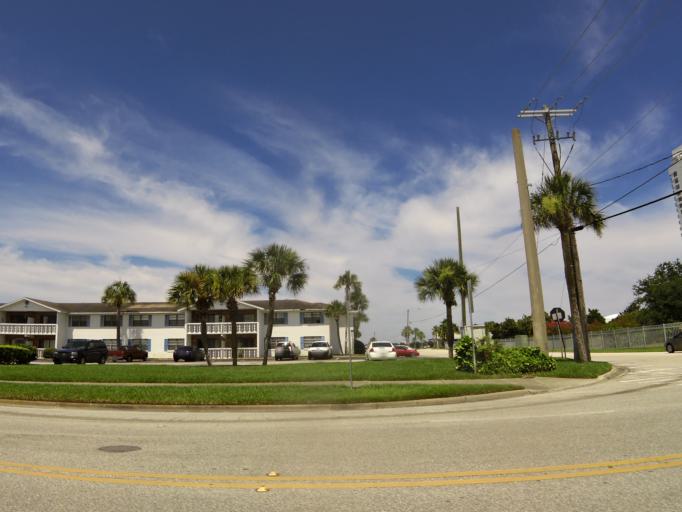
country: US
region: Florida
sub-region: Volusia County
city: Holly Hill
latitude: 29.2336
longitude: -81.0299
